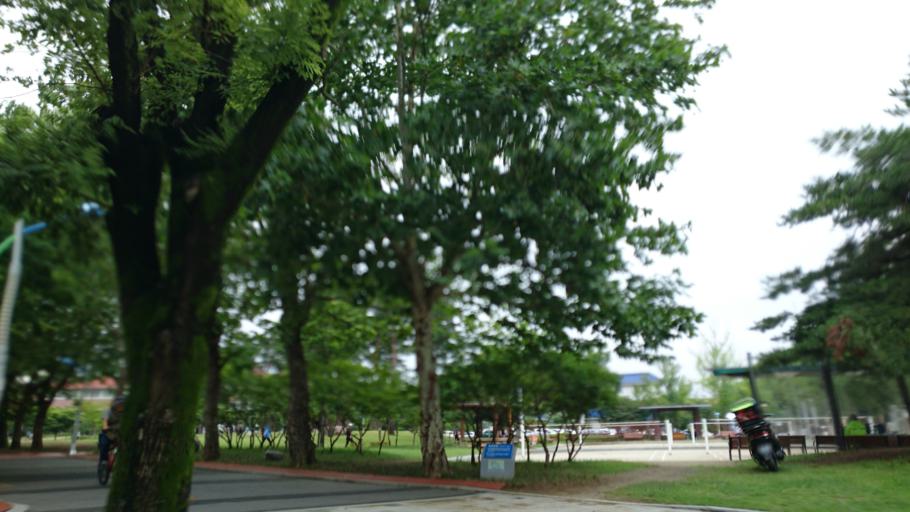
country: KR
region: Daegu
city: Daegu
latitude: 35.8709
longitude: 128.6408
